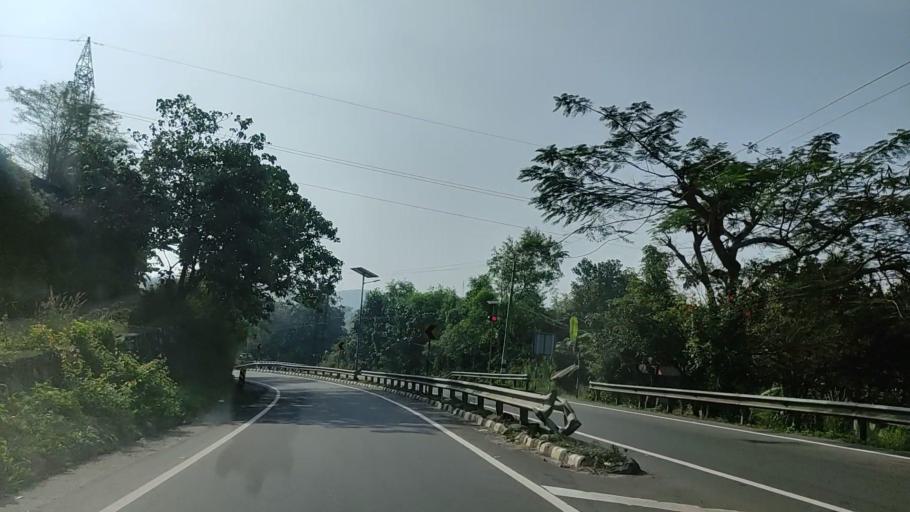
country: IN
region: Kerala
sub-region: Kollam
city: Punalur
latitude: 8.9770
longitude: 76.8145
